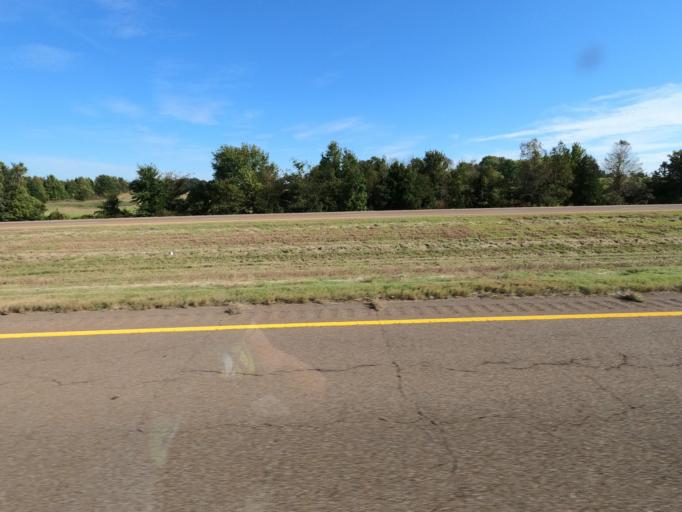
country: US
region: Tennessee
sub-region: Dyer County
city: Newbern
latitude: 36.1769
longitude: -89.2272
